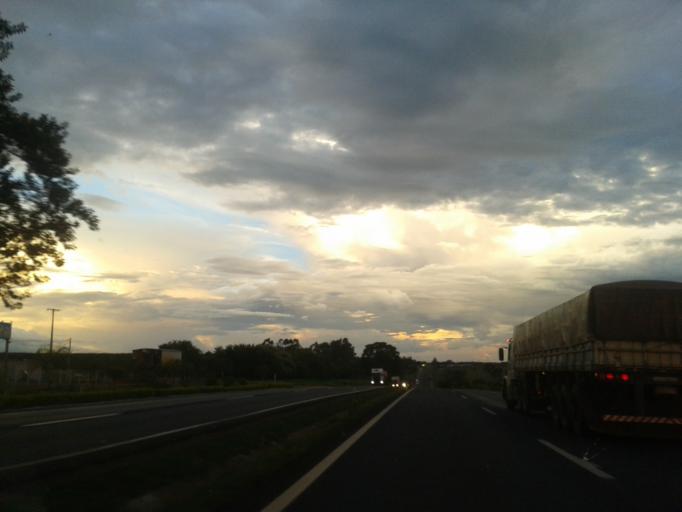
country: BR
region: Minas Gerais
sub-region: Centralina
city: Centralina
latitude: -18.7275
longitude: -49.1147
